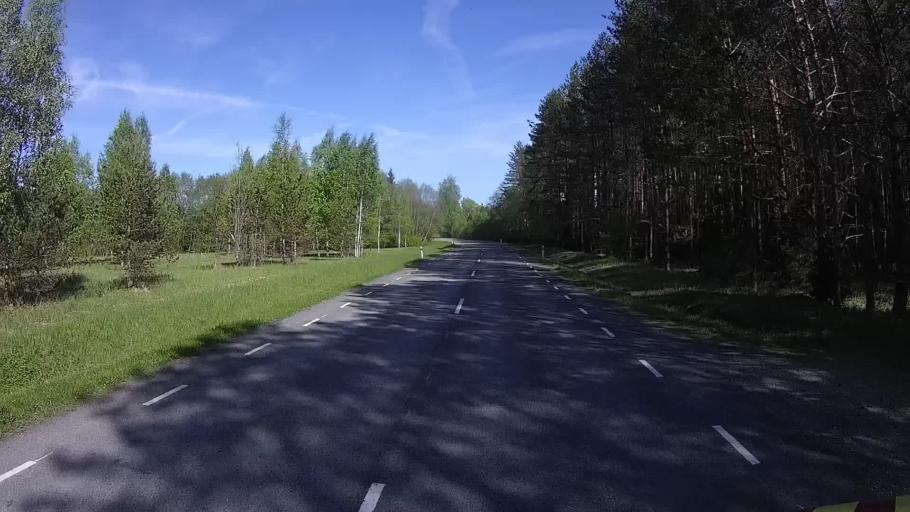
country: EE
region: Vorumaa
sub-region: Antsla vald
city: Vana-Antsla
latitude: 57.9487
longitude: 26.4072
